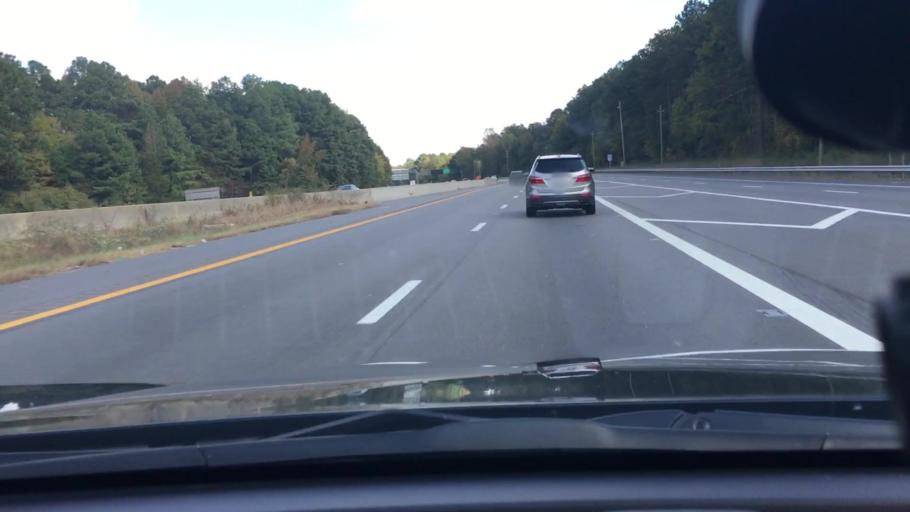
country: US
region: North Carolina
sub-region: Wake County
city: Garner
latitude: 35.7533
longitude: -78.5888
